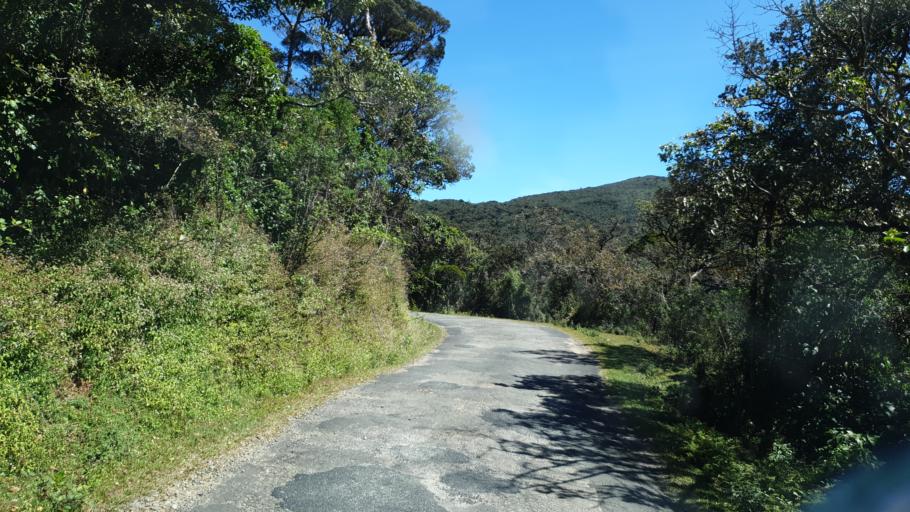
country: LK
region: Central
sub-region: Nuwara Eliya District
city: Nuwara Eliya
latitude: 6.8331
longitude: 80.8084
